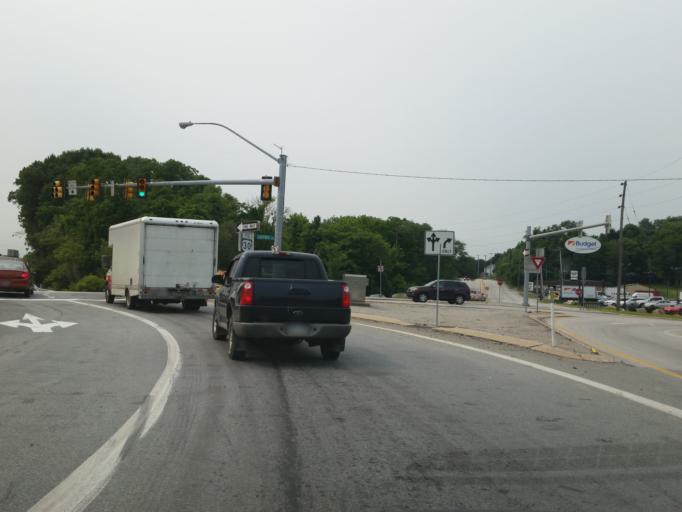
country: US
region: Pennsylvania
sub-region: York County
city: North York
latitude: 39.9912
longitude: -76.7354
